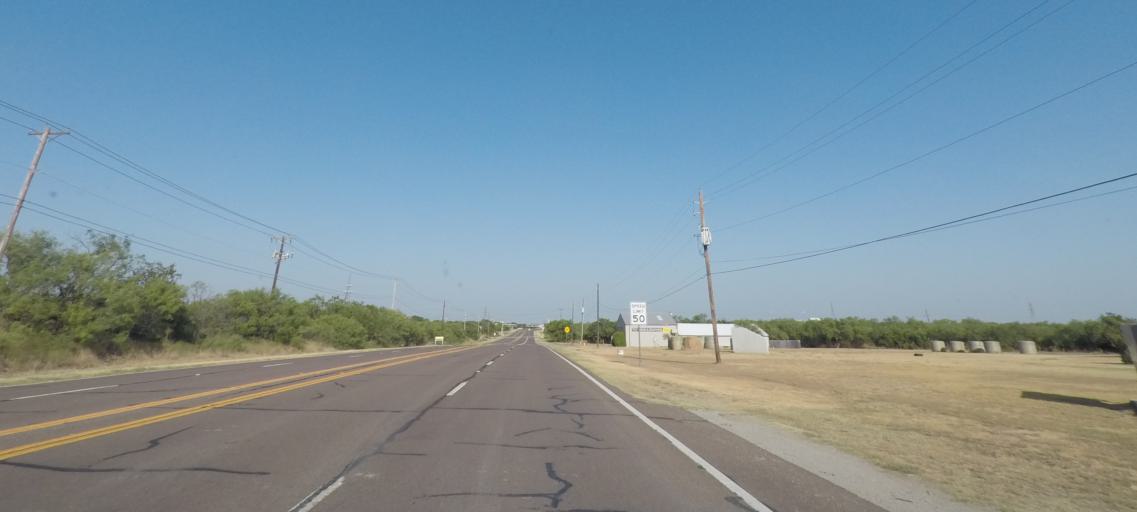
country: US
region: Texas
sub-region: Archer County
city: Holliday
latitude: 33.8593
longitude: -98.5960
